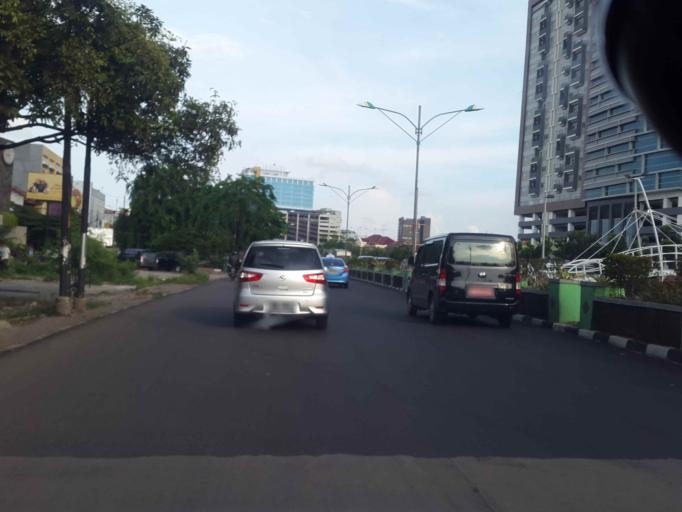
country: ID
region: West Java
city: Bekasi
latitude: -6.2482
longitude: 106.9846
